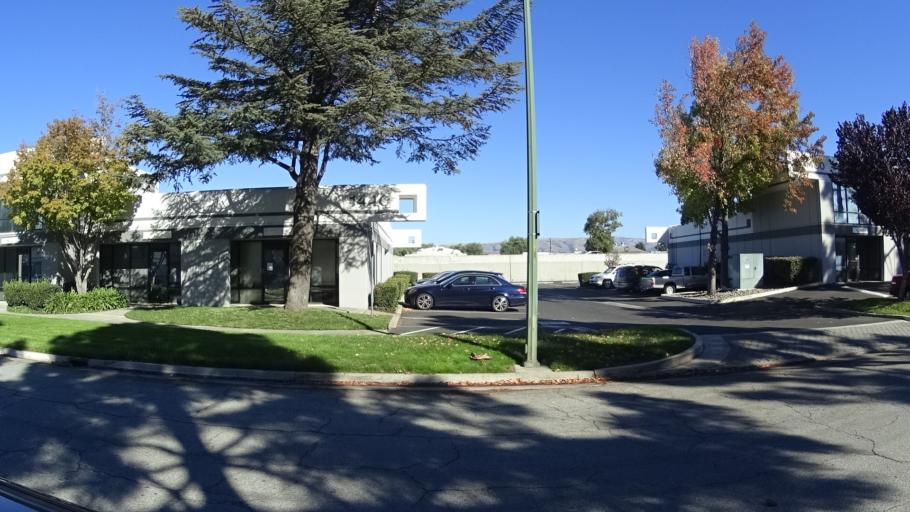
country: US
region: California
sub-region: Santa Clara County
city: San Jose
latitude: 37.3656
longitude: -121.9063
